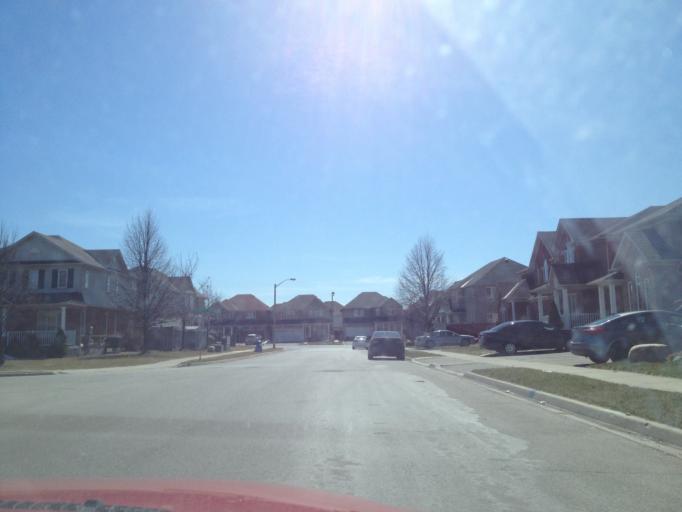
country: CA
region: Ontario
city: Brampton
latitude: 43.6884
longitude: -79.8181
